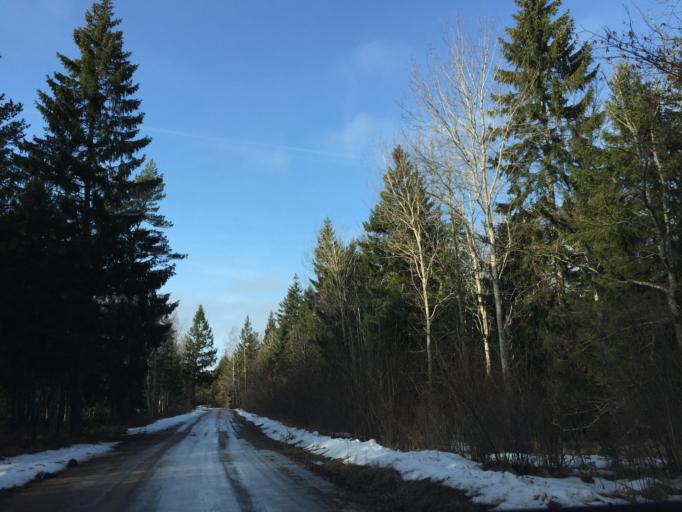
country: EE
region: Saare
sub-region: Kuressaare linn
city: Kuressaare
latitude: 58.4684
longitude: 21.9812
